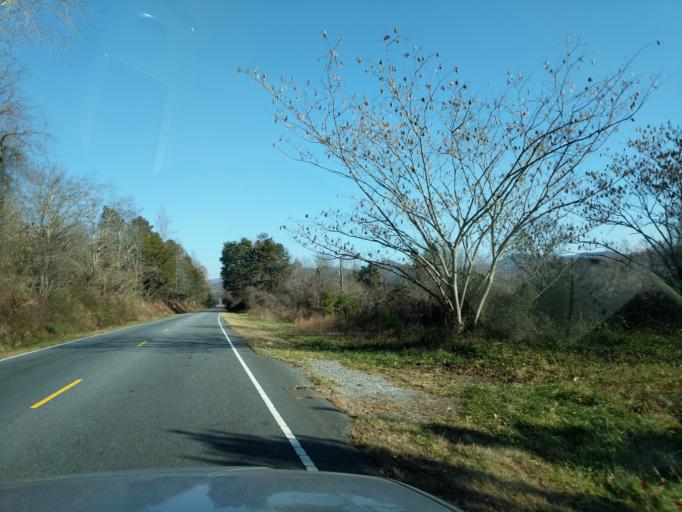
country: US
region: North Carolina
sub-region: Rutherford County
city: Rutherfordton
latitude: 35.4973
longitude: -81.9782
